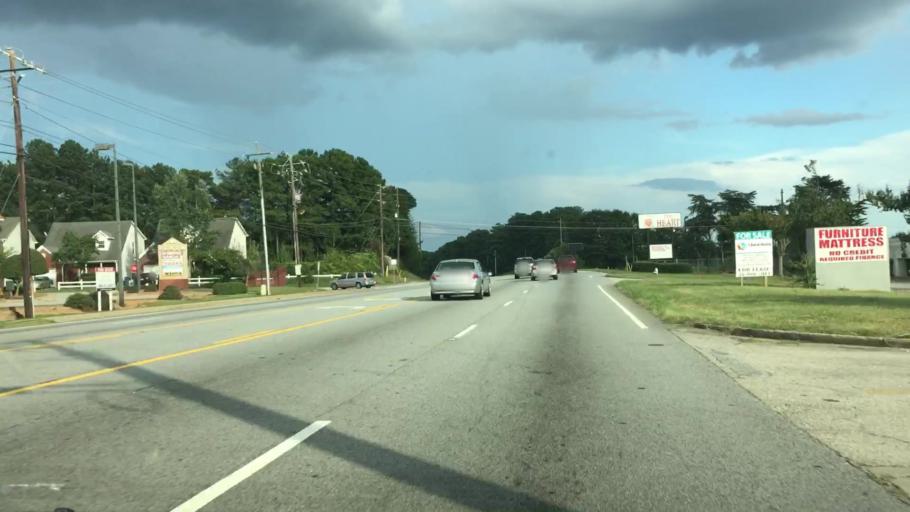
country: US
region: Georgia
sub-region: Clayton County
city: Riverdale
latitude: 33.5483
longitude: -84.4121
